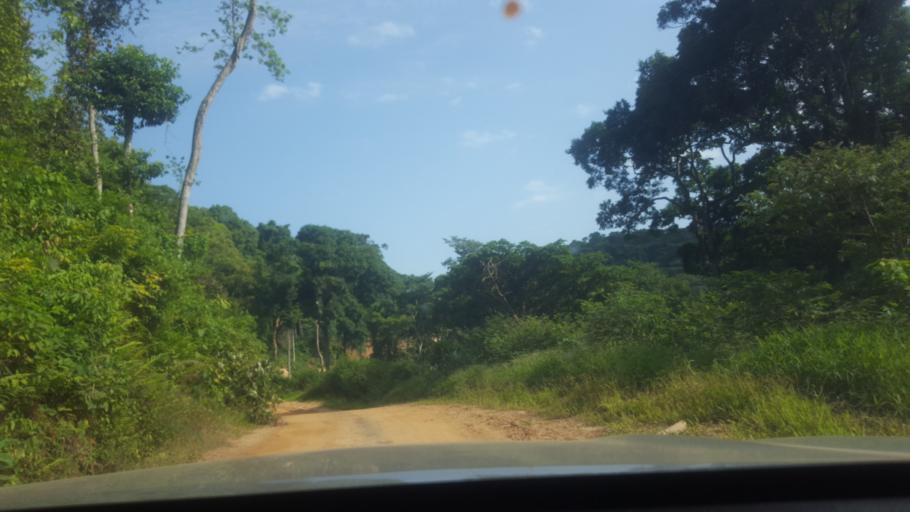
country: ET
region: Southern Nations, Nationalities, and People's Region
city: Tippi
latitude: 7.5350
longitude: 34.9836
